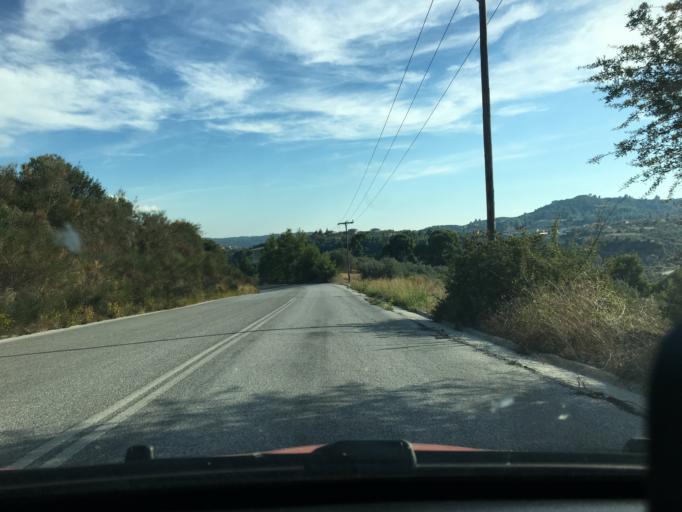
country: GR
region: Central Macedonia
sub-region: Nomos Chalkidikis
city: Agios Nikolaos
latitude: 40.2612
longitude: 23.6989
